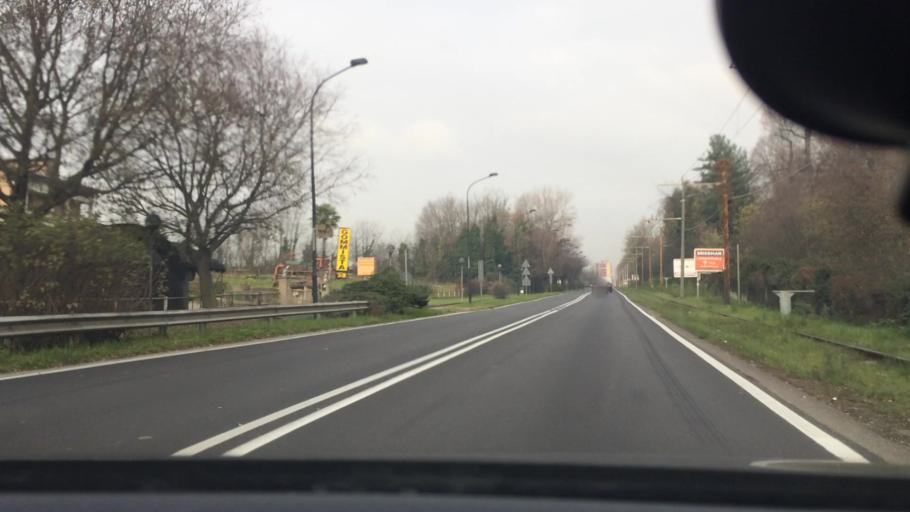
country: IT
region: Lombardy
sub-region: Provincia di Monza e Brianza
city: Limbiate
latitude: 45.6080
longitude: 9.1217
